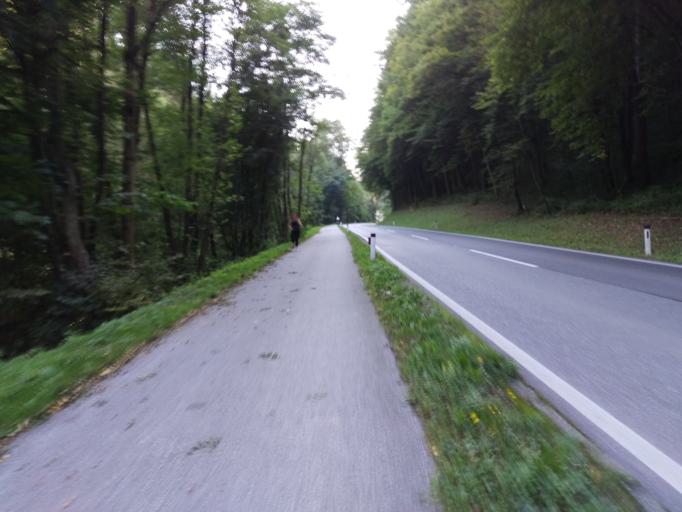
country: AT
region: Styria
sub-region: Politischer Bezirk Graz-Umgebung
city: Thal
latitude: 47.0825
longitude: 15.3681
